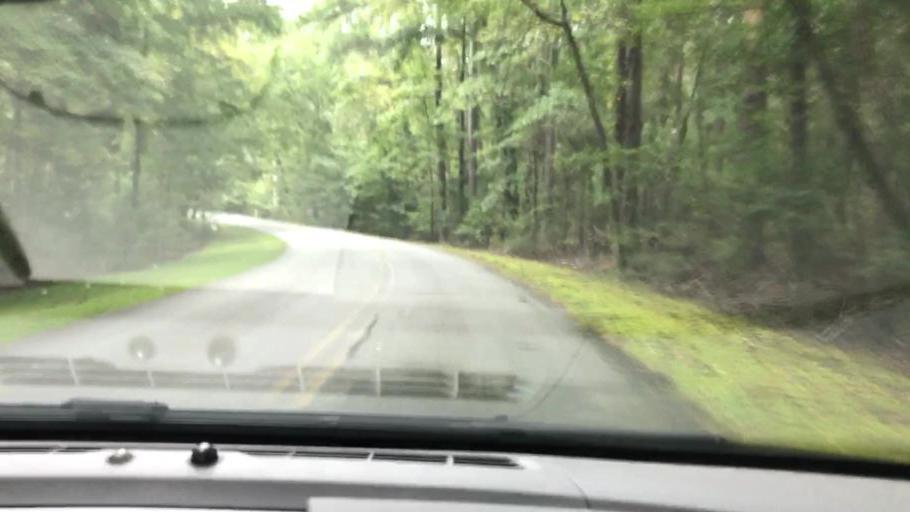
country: US
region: Georgia
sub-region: Clay County
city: Fort Gaines
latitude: 31.6671
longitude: -85.0556
